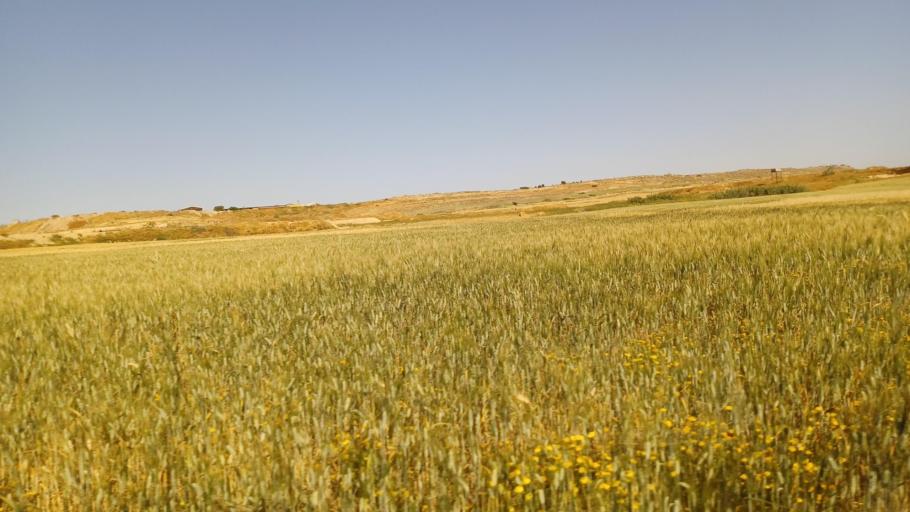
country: CY
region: Lefkosia
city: Mammari
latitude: 35.1562
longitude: 33.2432
